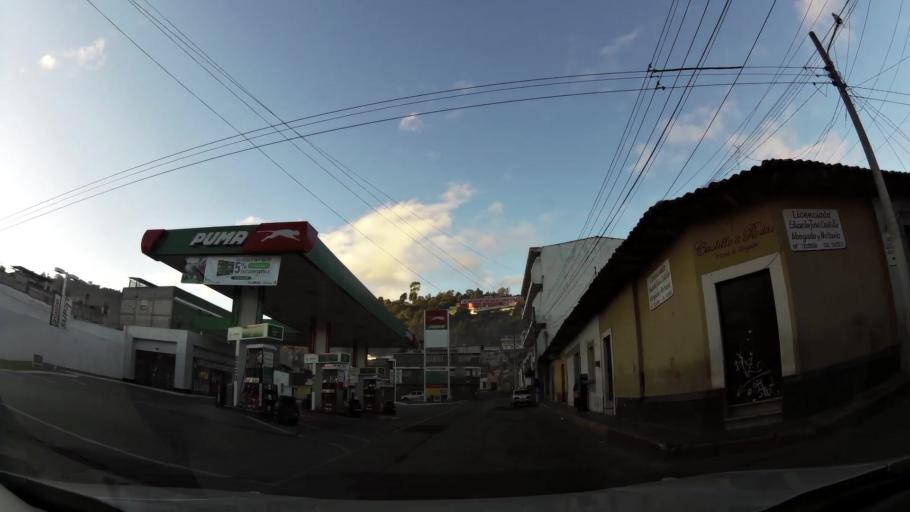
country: GT
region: Quetzaltenango
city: Quetzaltenango
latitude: 14.8324
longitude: -91.5193
